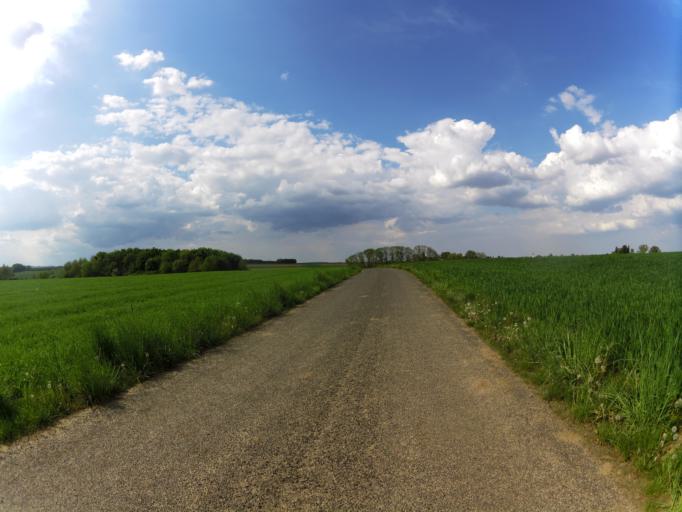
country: DE
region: Bavaria
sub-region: Regierungsbezirk Unterfranken
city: Giebelstadt
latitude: 49.6214
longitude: 9.9412
